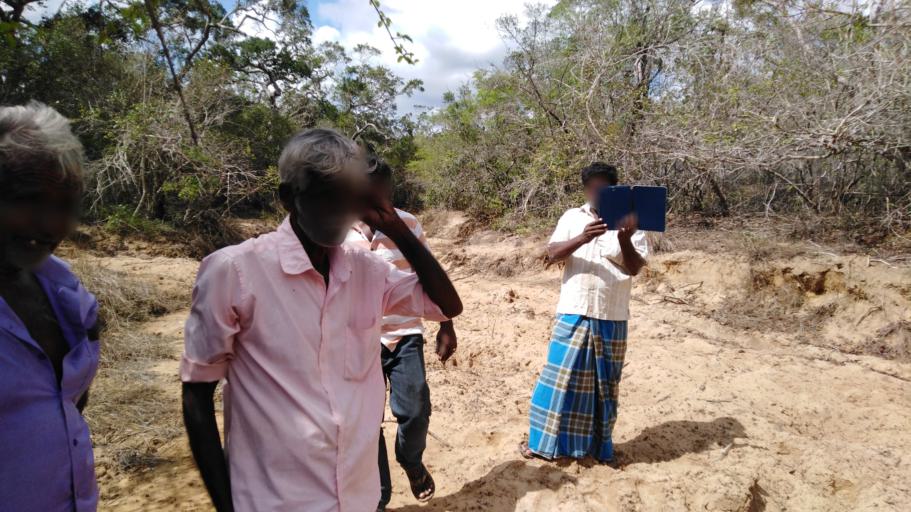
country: LK
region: Northern Province
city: Kilinochchi
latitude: 9.2816
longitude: 80.2856
